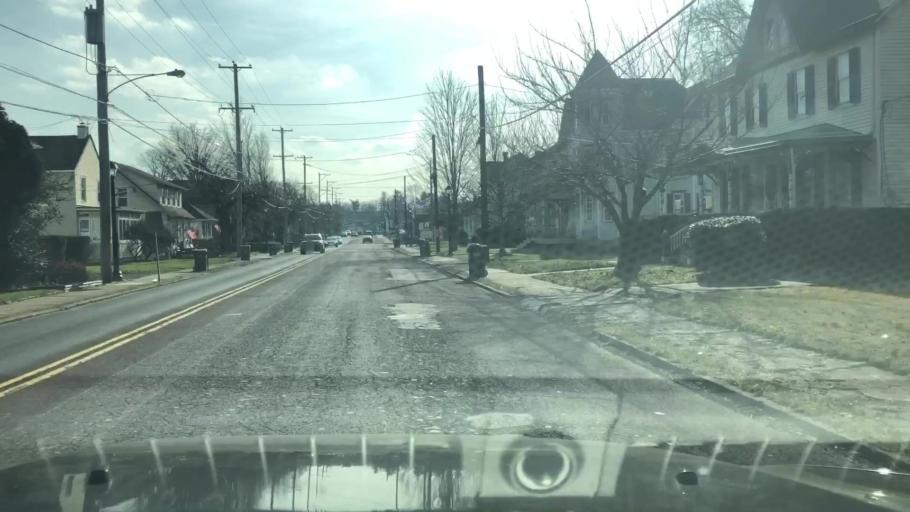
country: US
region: Pennsylvania
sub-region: Bucks County
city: Langhorne
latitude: 40.1801
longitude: -74.9184
